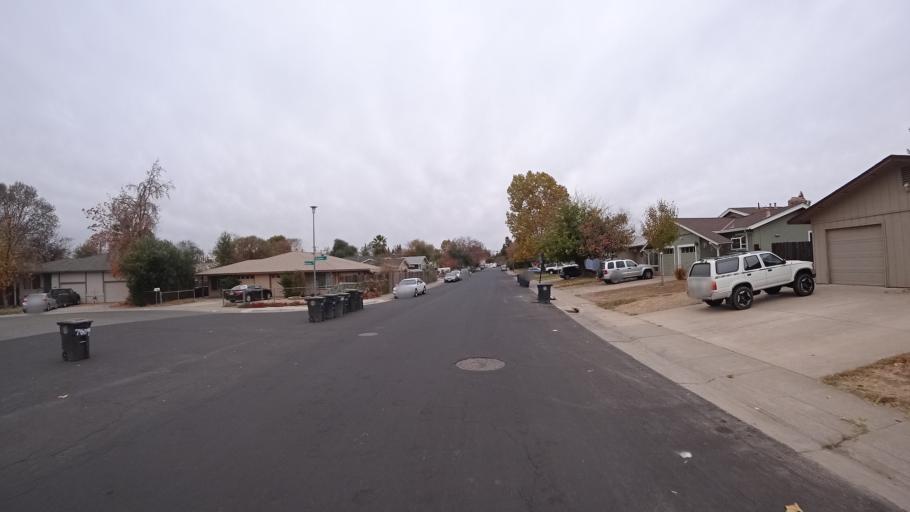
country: US
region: California
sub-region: Sacramento County
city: Citrus Heights
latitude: 38.7028
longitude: -121.3043
